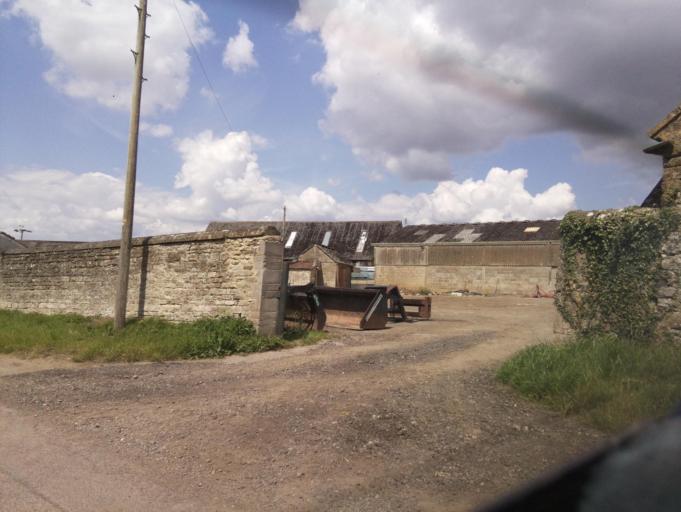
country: GB
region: England
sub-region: Oxfordshire
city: Shrivenham
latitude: 51.5848
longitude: -1.6717
